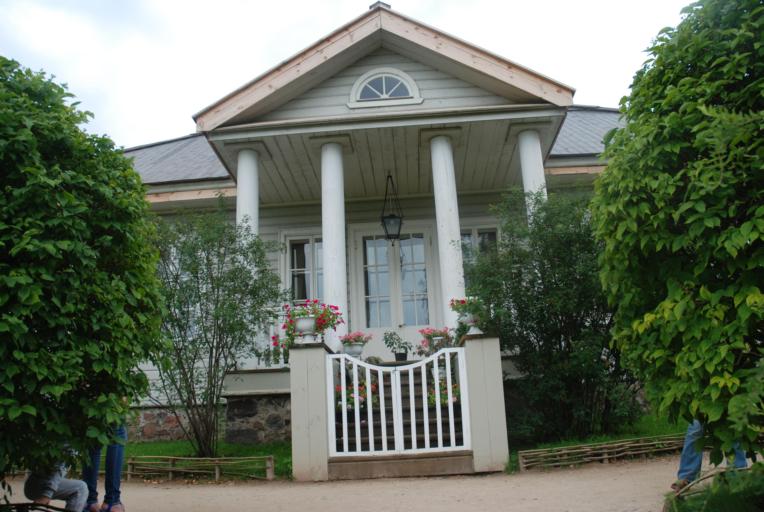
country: RU
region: Pskov
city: Pushkinskiye Gory
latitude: 57.0612
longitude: 28.9193
